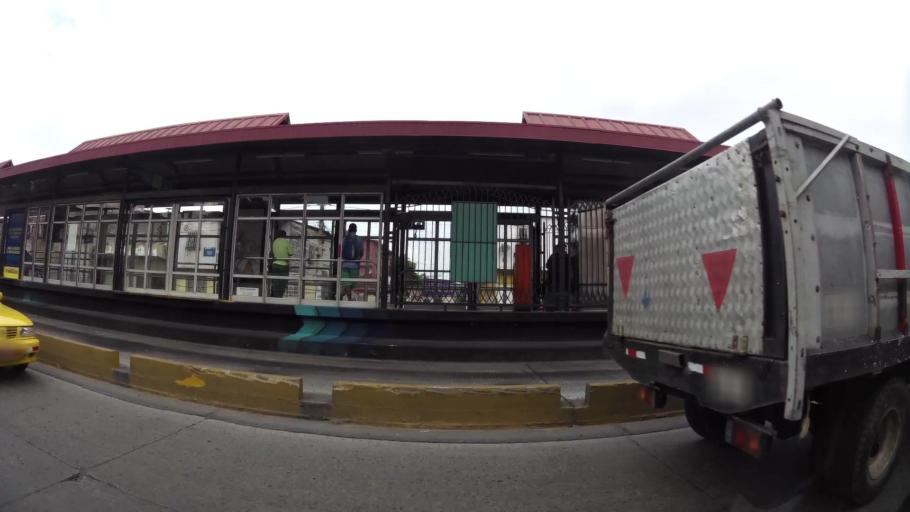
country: EC
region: Guayas
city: Guayaquil
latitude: -2.2550
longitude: -79.8795
